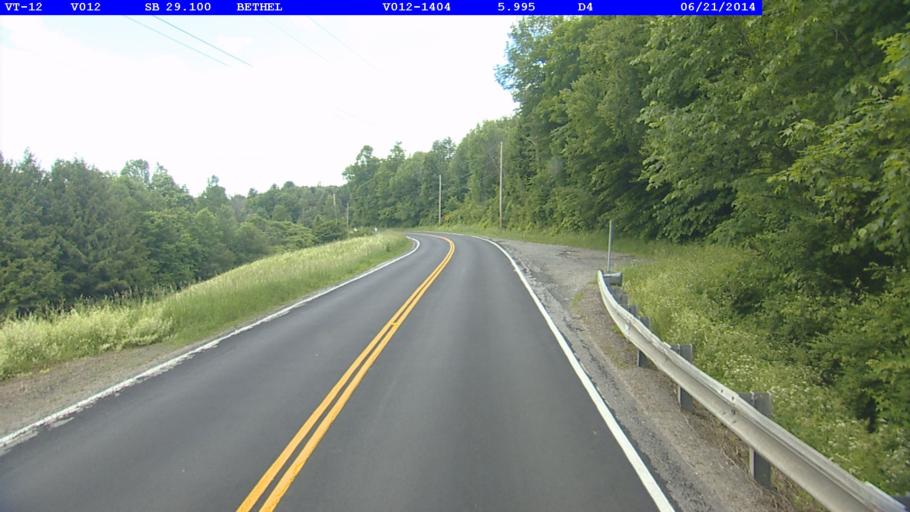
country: US
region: Vermont
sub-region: Orange County
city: Randolph
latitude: 43.8818
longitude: -72.6456
